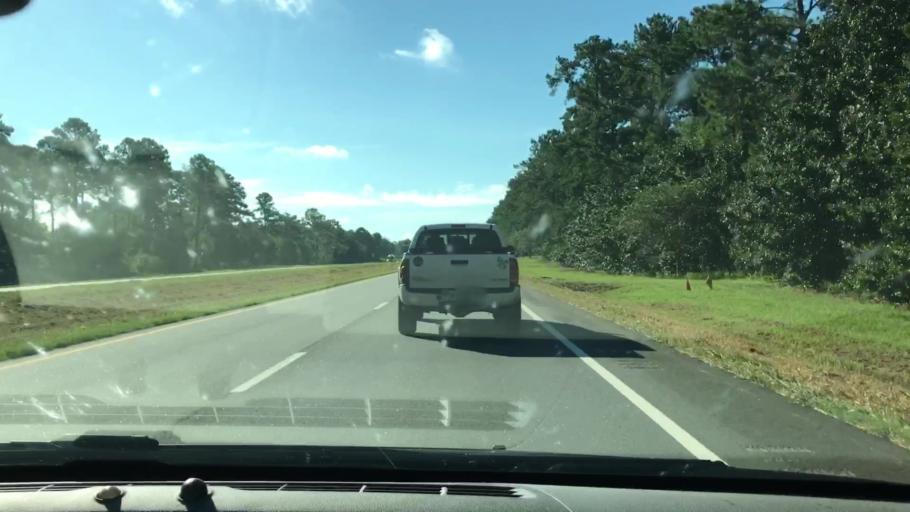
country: US
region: Georgia
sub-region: Lee County
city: Leesburg
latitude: 31.6510
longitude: -84.2647
